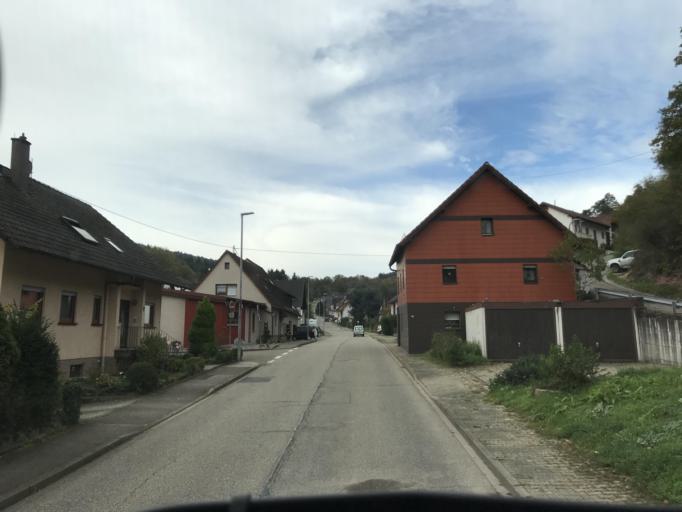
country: DE
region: Baden-Wuerttemberg
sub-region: Karlsruhe Region
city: Gaggenau
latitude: 48.7810
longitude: 8.3052
